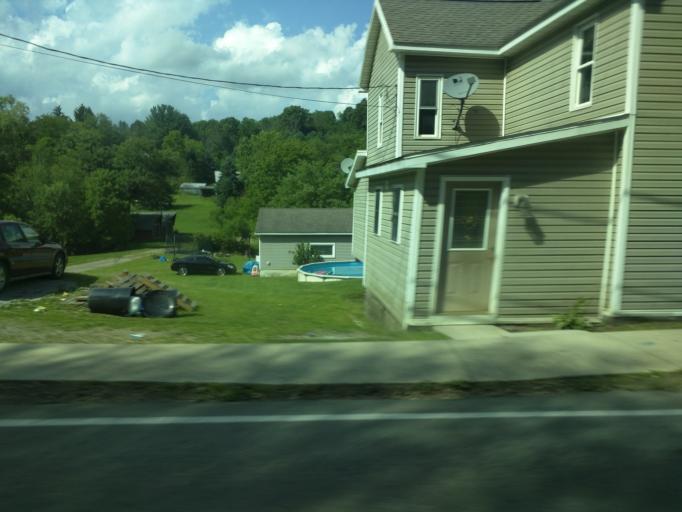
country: US
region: Pennsylvania
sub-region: Indiana County
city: Chevy Chase Heights
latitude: 40.7950
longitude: -79.1707
